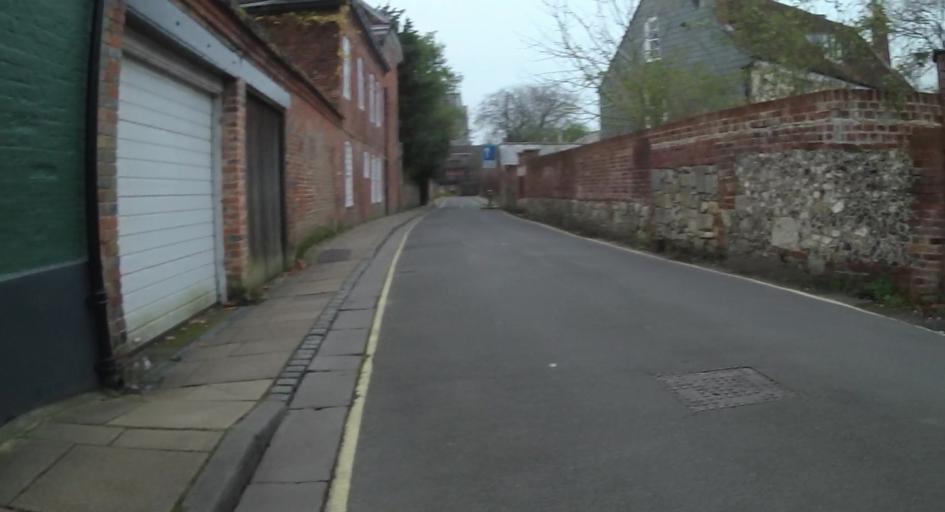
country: GB
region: England
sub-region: Hampshire
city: Winchester
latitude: 51.0602
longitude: -1.3104
